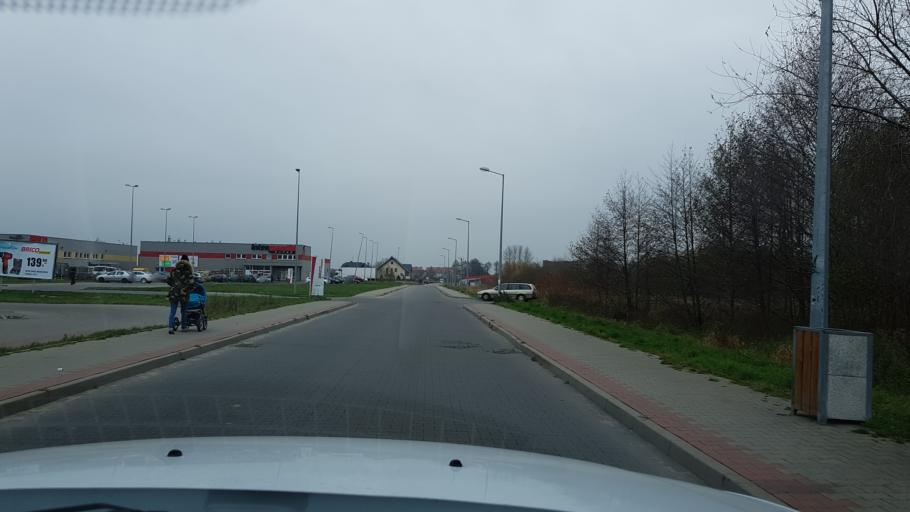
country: PL
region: West Pomeranian Voivodeship
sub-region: Powiat slawienski
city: Darlowo
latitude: 54.4192
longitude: 16.4160
